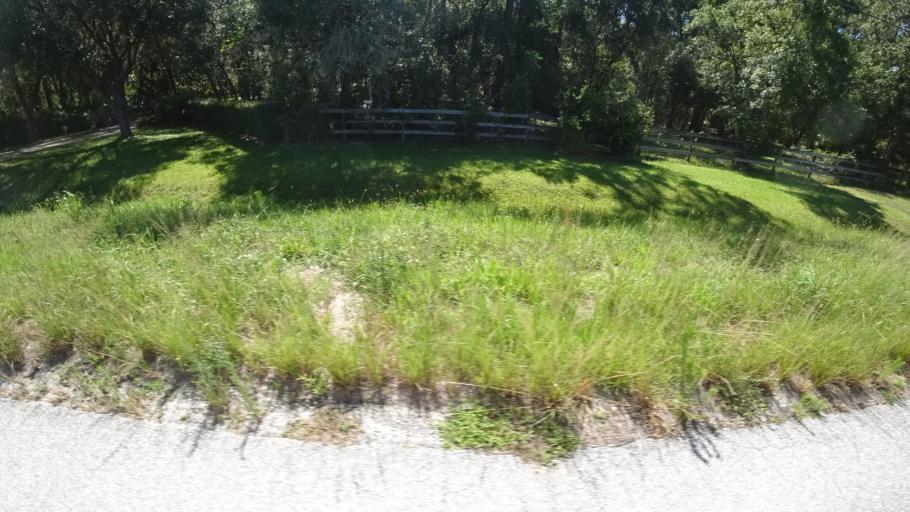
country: US
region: Florida
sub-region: Sarasota County
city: The Meadows
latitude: 27.4689
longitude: -82.3031
